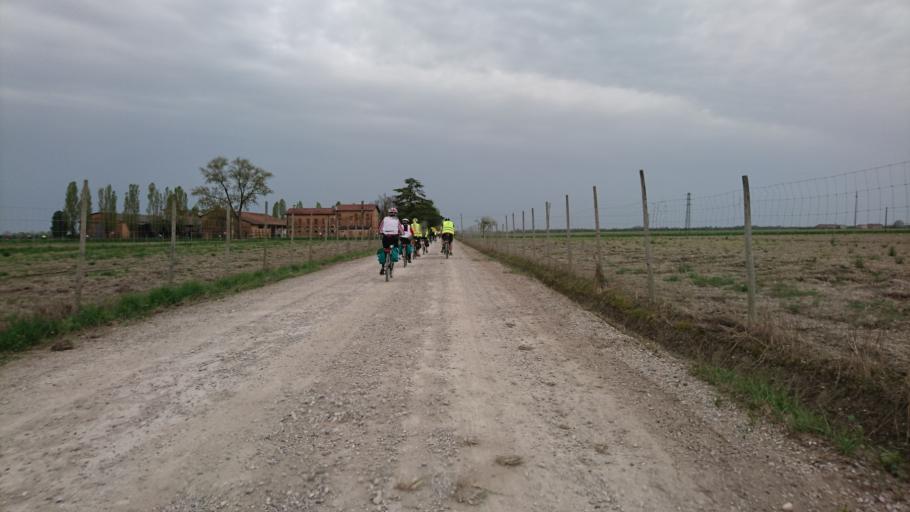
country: IT
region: Veneto
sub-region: Provincia di Venezia
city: Lugugnana
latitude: 45.6887
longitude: 12.9313
